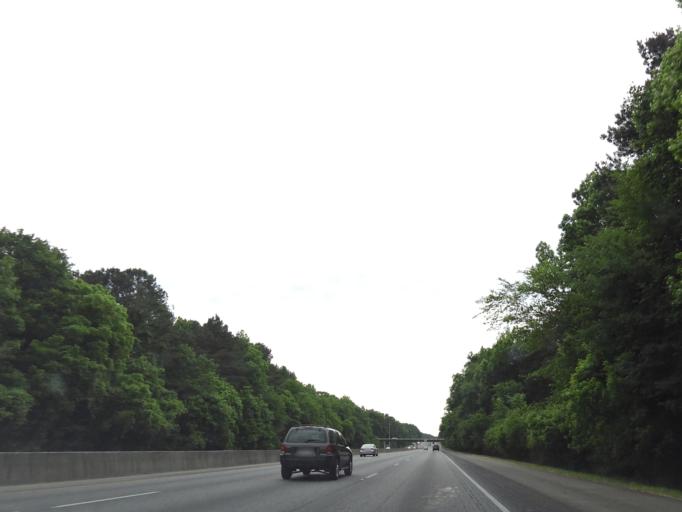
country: US
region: Georgia
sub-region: Bibb County
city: West Point
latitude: 32.8971
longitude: -83.7835
